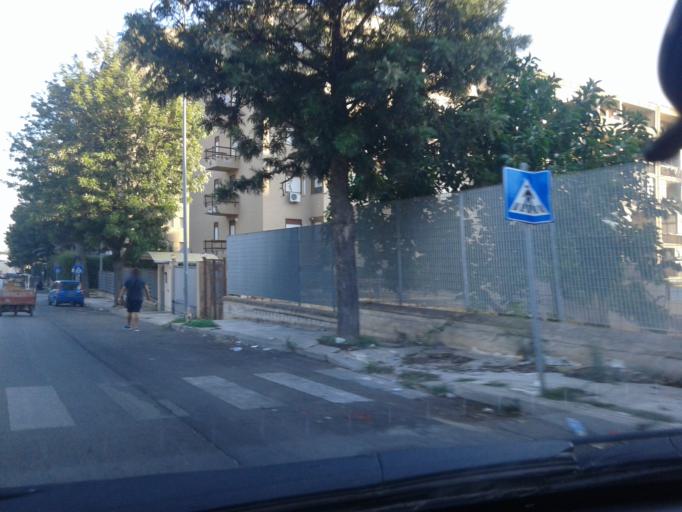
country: IT
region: Sicily
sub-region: Palermo
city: Ciaculli
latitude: 38.0843
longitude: 13.3622
